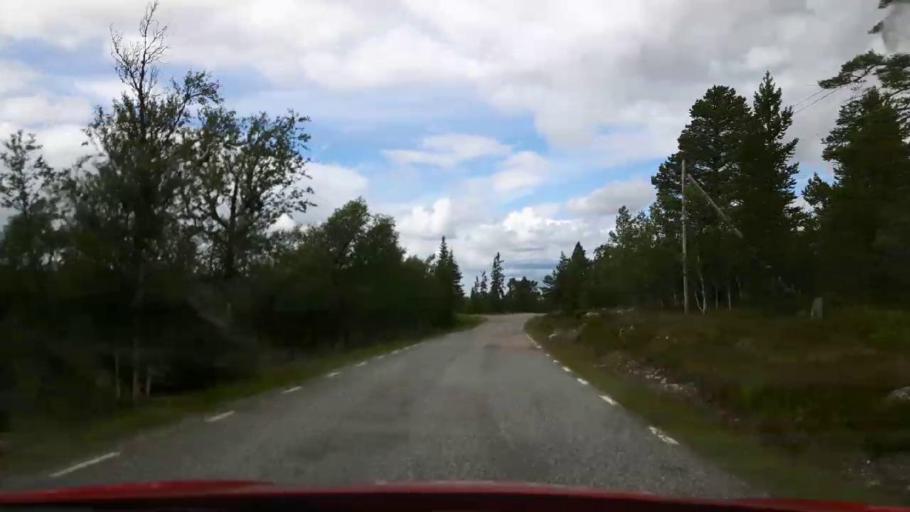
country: NO
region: Hedmark
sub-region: Engerdal
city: Engerdal
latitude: 62.3356
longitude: 12.8012
